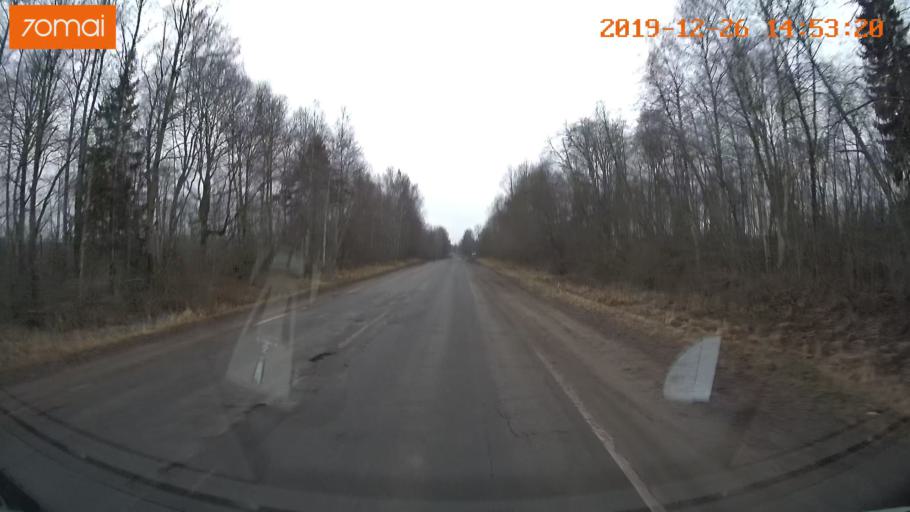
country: RU
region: Jaroslavl
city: Rybinsk
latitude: 58.3160
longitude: 38.8899
